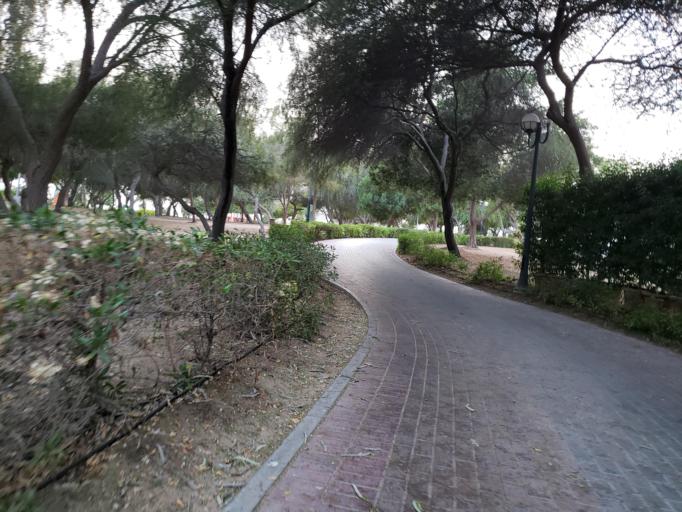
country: AE
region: Ash Shariqah
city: Sharjah
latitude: 25.3183
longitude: 55.3494
